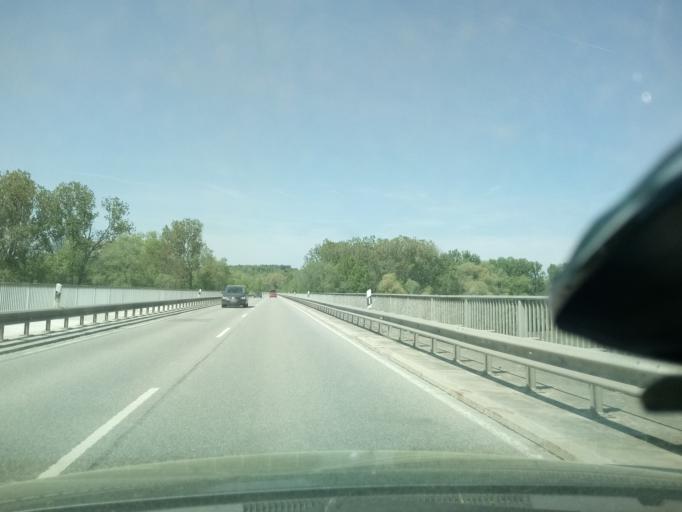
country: DE
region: Bavaria
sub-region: Upper Bavaria
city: Kraiburg am Inn
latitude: 48.1924
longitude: 12.4337
